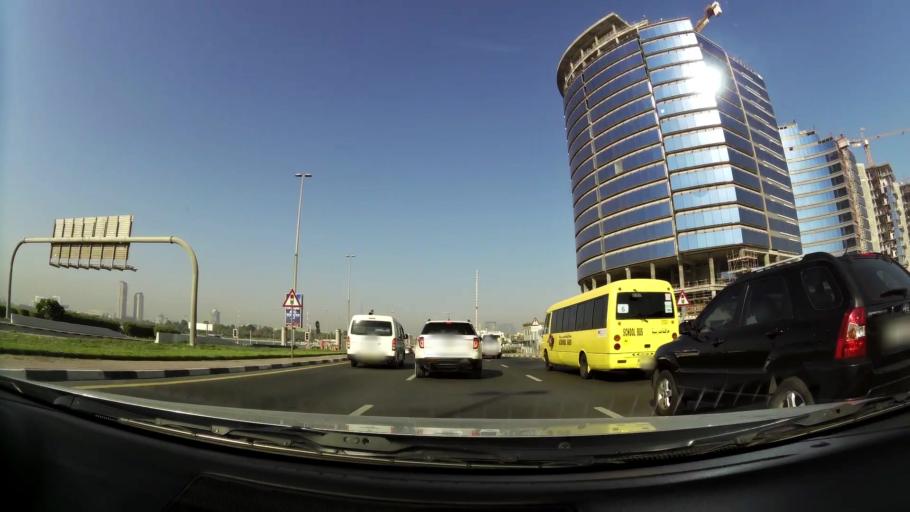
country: AE
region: Ash Shariqah
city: Sharjah
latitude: 25.2506
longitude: 55.3278
